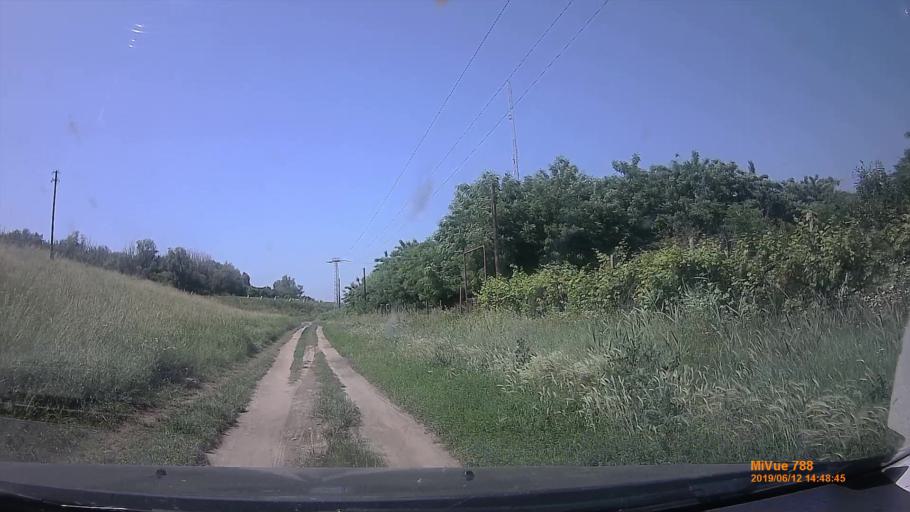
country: HU
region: Csongrad
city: Mako
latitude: 46.2043
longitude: 20.4666
